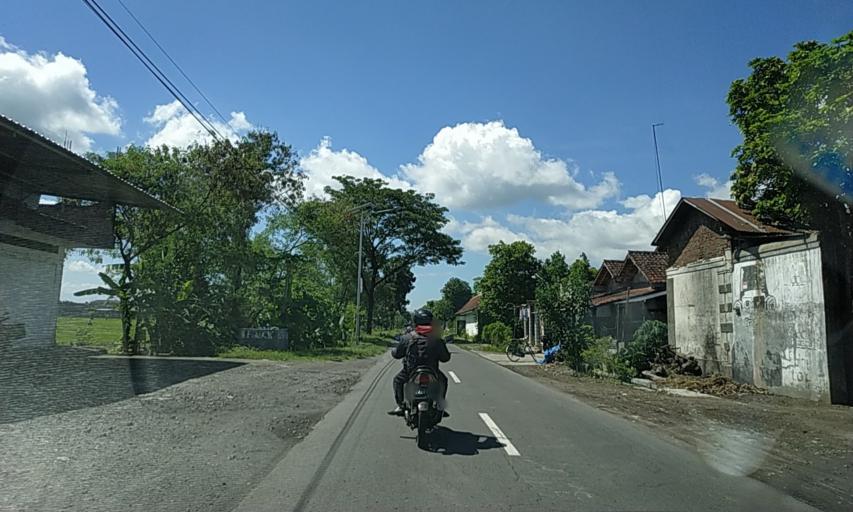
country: ID
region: Central Java
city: Trucuk
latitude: -7.7322
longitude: 110.6971
